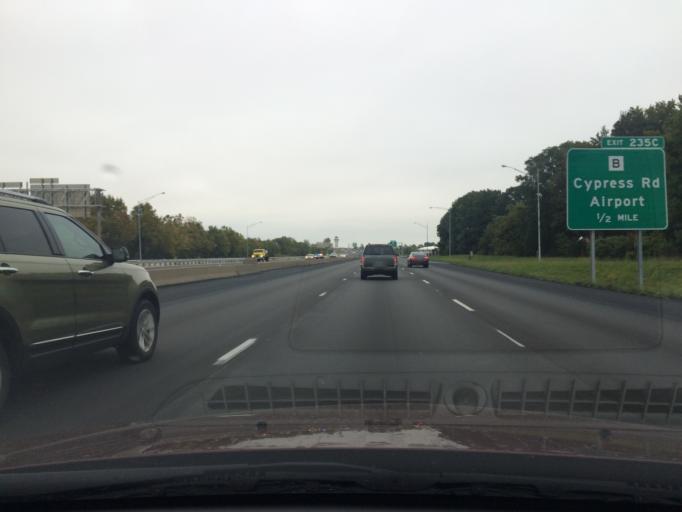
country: US
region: Missouri
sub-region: Saint Louis County
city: Saint Ann
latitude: 38.7434
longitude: -90.3928
